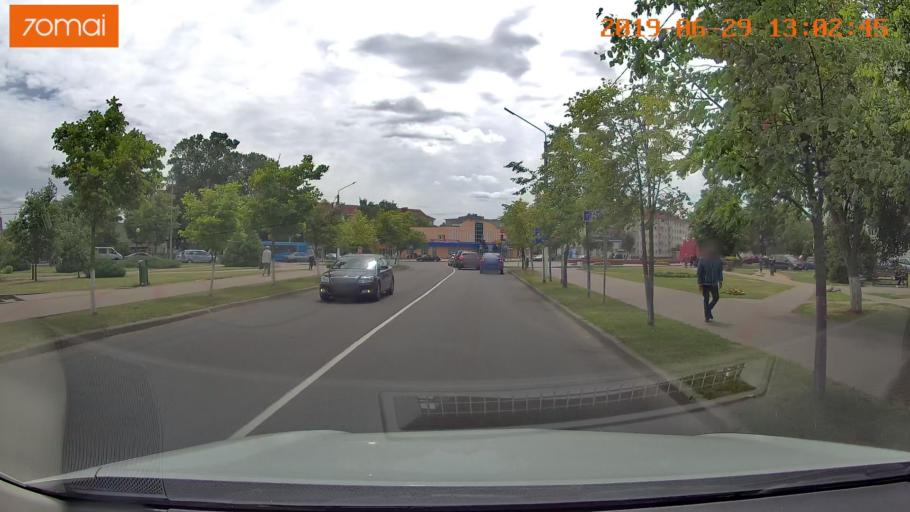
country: BY
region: Minsk
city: Slutsk
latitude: 53.0344
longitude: 27.5599
